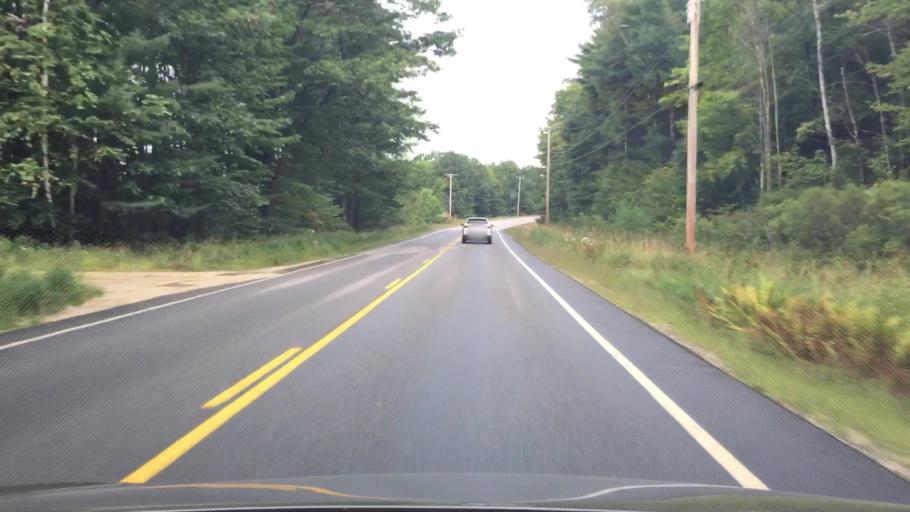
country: US
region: Maine
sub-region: Oxford County
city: Hartford
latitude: 44.3627
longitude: -70.3140
